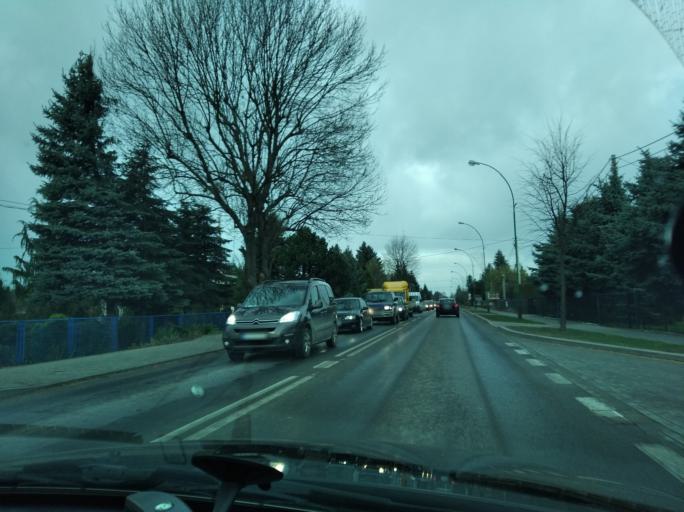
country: PL
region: Subcarpathian Voivodeship
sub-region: Powiat lancucki
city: Lancut
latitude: 50.0838
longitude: 22.2326
